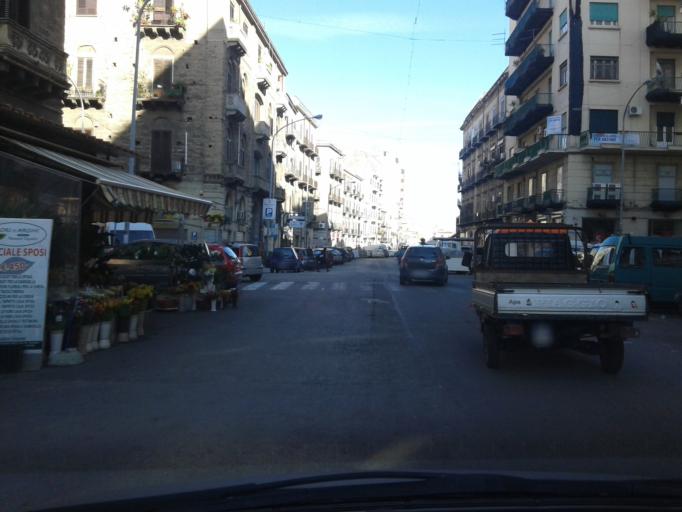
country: IT
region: Sicily
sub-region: Palermo
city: Palermo
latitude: 38.1186
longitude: 13.3479
